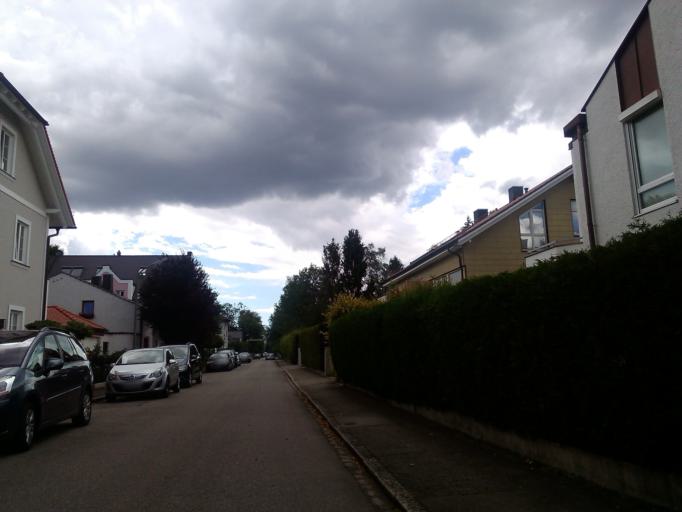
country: DE
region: Bavaria
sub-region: Upper Bavaria
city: Pasing
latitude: 48.1365
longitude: 11.4475
